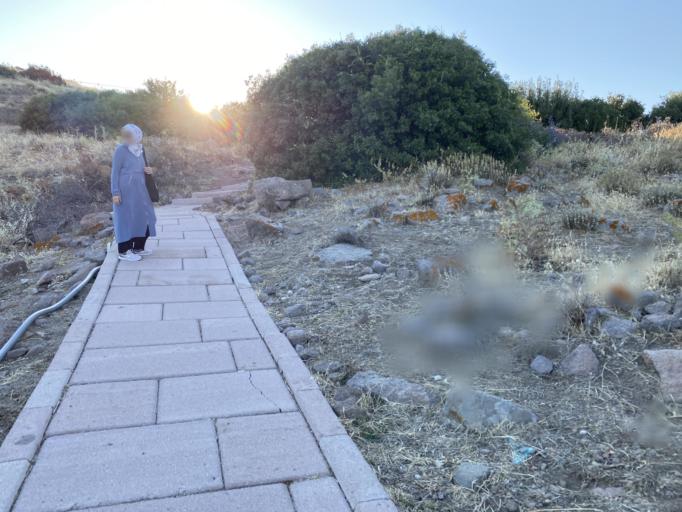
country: TR
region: Canakkale
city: Behram
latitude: 39.4915
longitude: 26.3385
